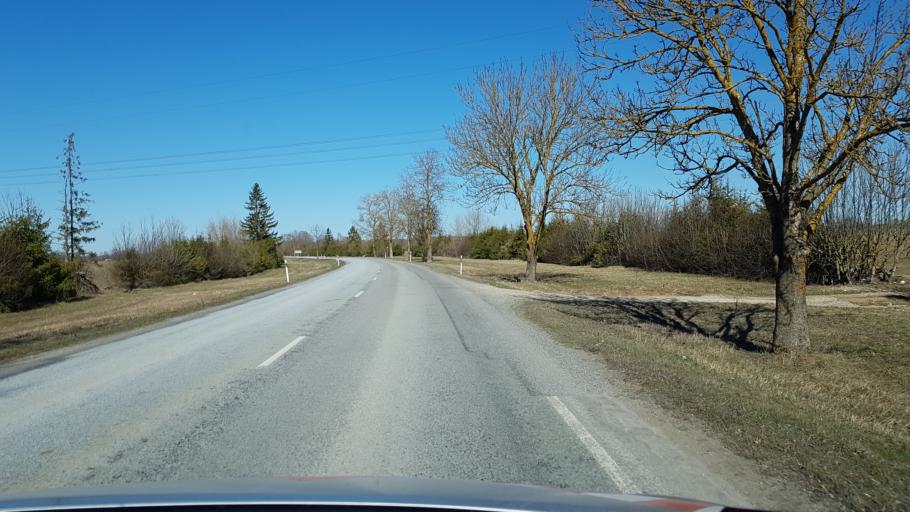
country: EE
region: Laeaene-Virumaa
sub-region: Rakvere linn
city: Rakvere
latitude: 59.3775
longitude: 26.3904
